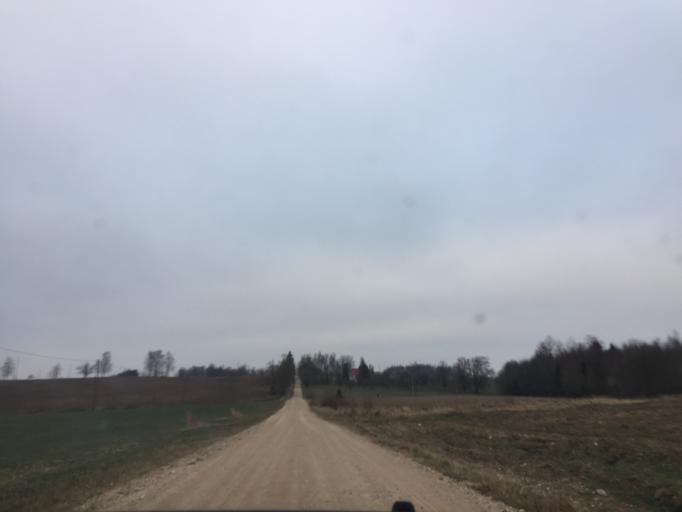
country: LV
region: Raunas
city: Rauna
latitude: 57.3012
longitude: 25.5846
